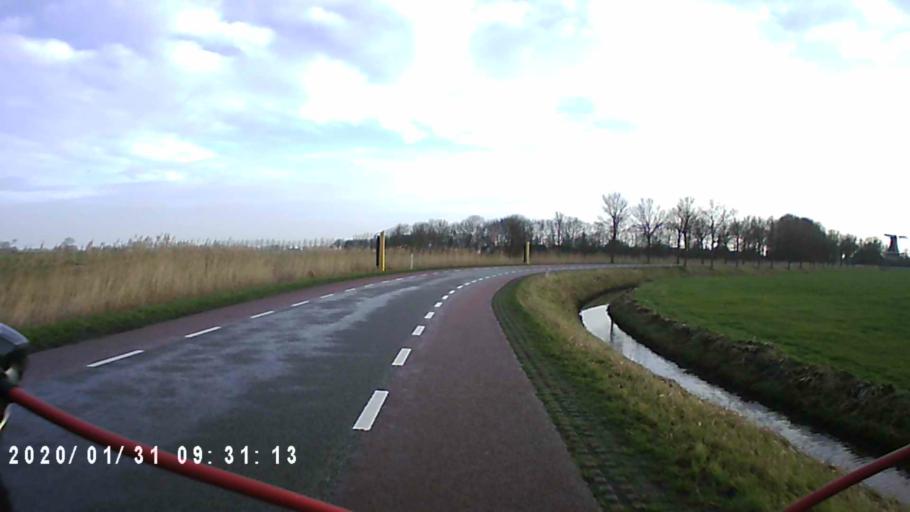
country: NL
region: Groningen
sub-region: Gemeente Zuidhorn
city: Aduard
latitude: 53.3053
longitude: 6.4592
